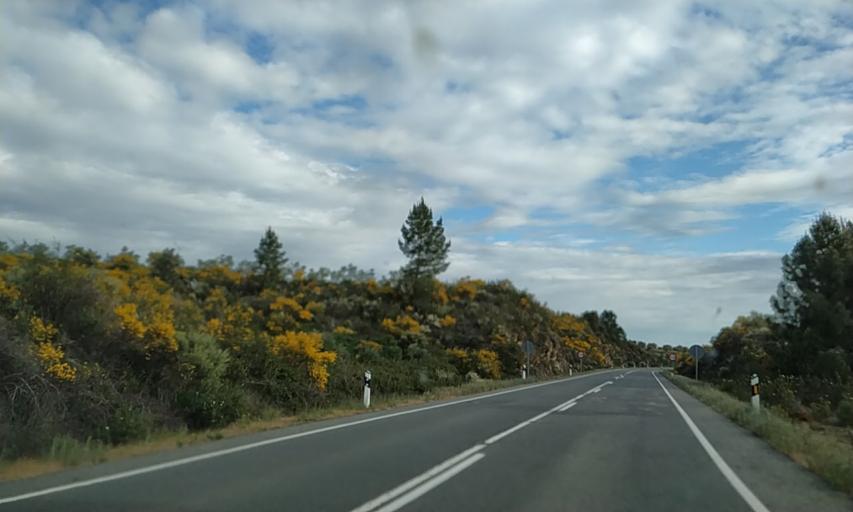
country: ES
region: Extremadura
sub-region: Provincia de Caceres
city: Perales del Puerto
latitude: 40.1363
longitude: -6.6795
